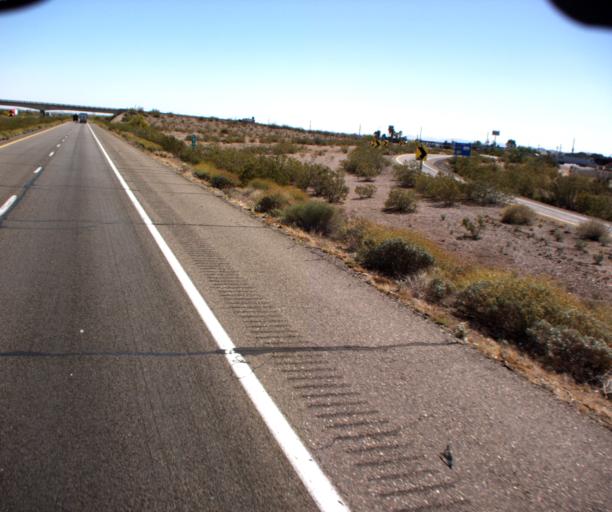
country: US
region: Arizona
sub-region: Maricopa County
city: Buckeye
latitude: 33.4979
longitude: -112.9402
